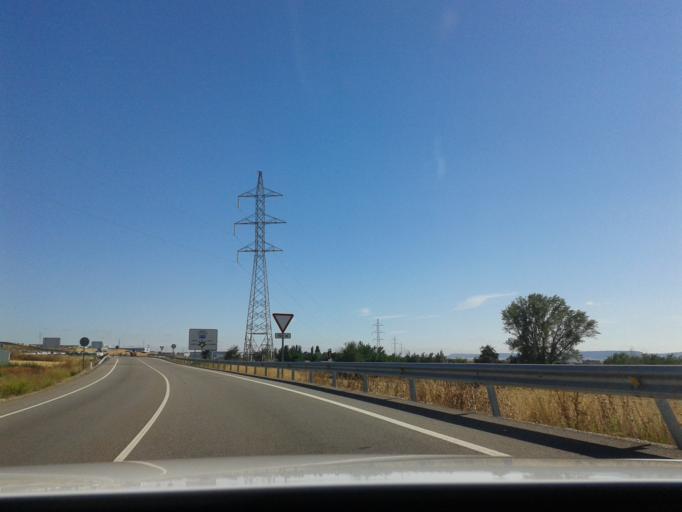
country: ES
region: Castille-La Mancha
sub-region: Provincia de Guadalajara
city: Alovera
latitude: 40.5964
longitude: -3.2585
